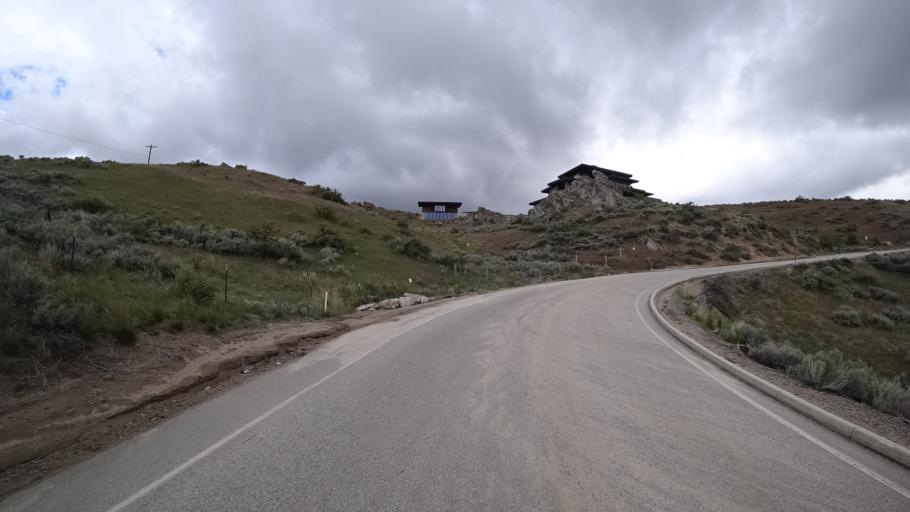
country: US
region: Idaho
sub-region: Ada County
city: Boise
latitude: 43.7115
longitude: -116.1635
